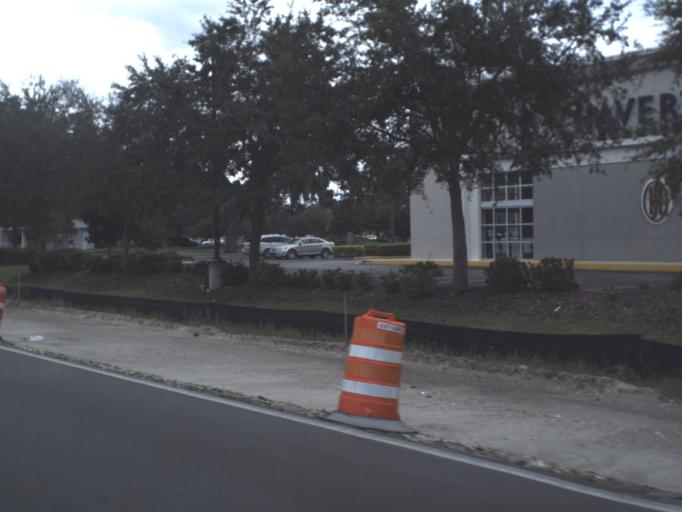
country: US
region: Florida
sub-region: Charlotte County
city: Port Charlotte
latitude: 27.0036
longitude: -82.1284
